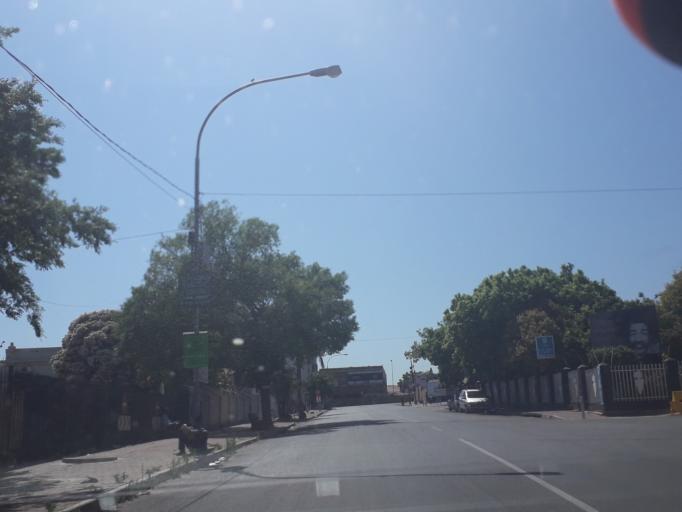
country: ZA
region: Gauteng
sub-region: City of Johannesburg Metropolitan Municipality
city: Johannesburg
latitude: -26.1572
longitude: 28.0836
